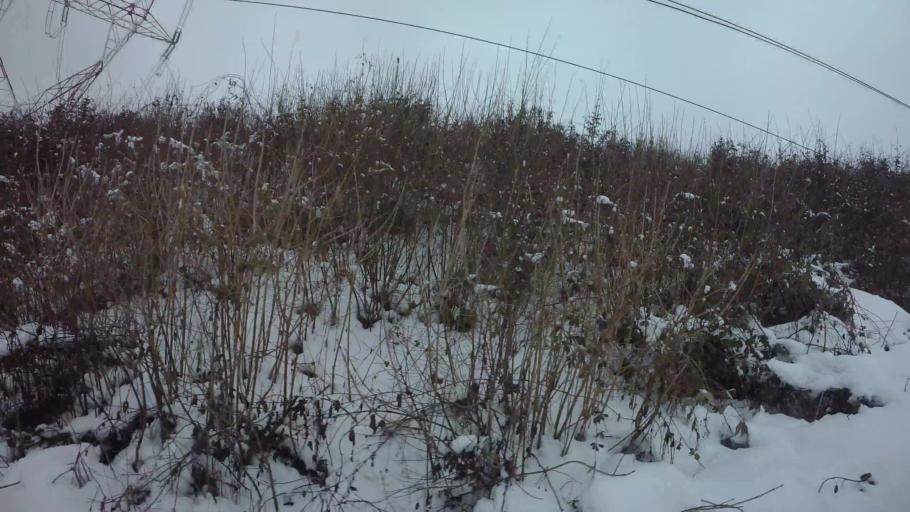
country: BA
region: Federation of Bosnia and Herzegovina
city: Hadzici
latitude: 43.8560
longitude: 18.2703
